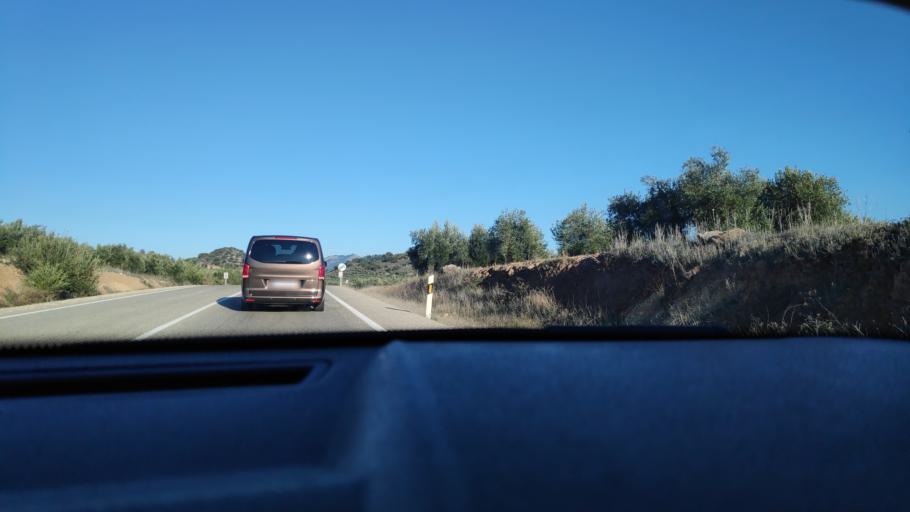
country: ES
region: Andalusia
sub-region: Province of Cordoba
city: Fuente-Tojar
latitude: 37.5648
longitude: -4.1838
